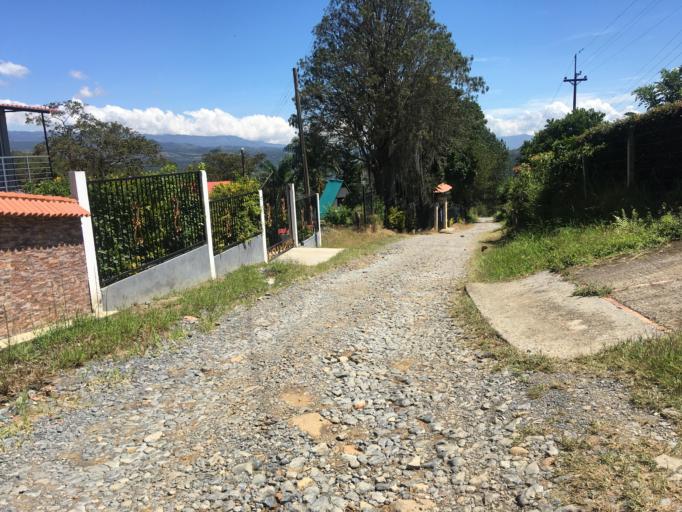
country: CO
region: Santander
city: Barbosa
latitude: 5.9116
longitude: -73.5984
